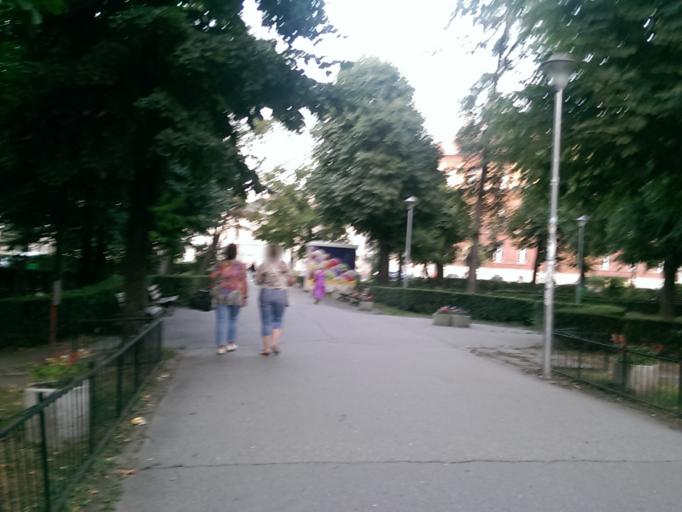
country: RO
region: Cluj
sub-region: Municipiul Cluj-Napoca
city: Cluj-Napoca
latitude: 46.7694
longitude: 23.5980
